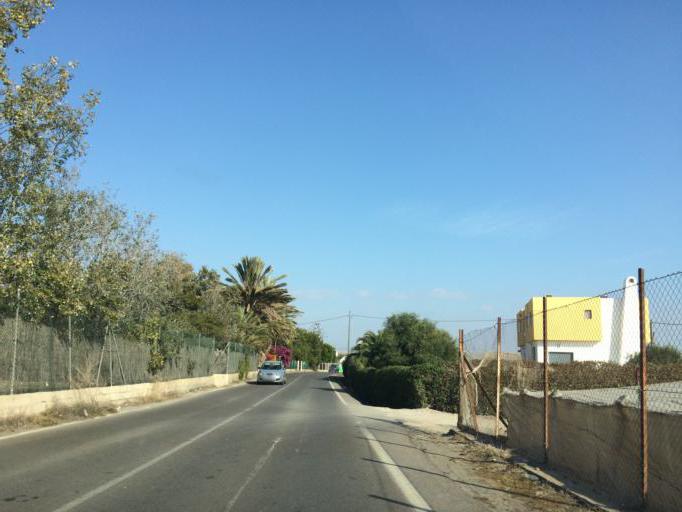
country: ES
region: Andalusia
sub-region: Provincia de Almeria
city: Almeria
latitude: 36.8455
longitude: -2.4248
